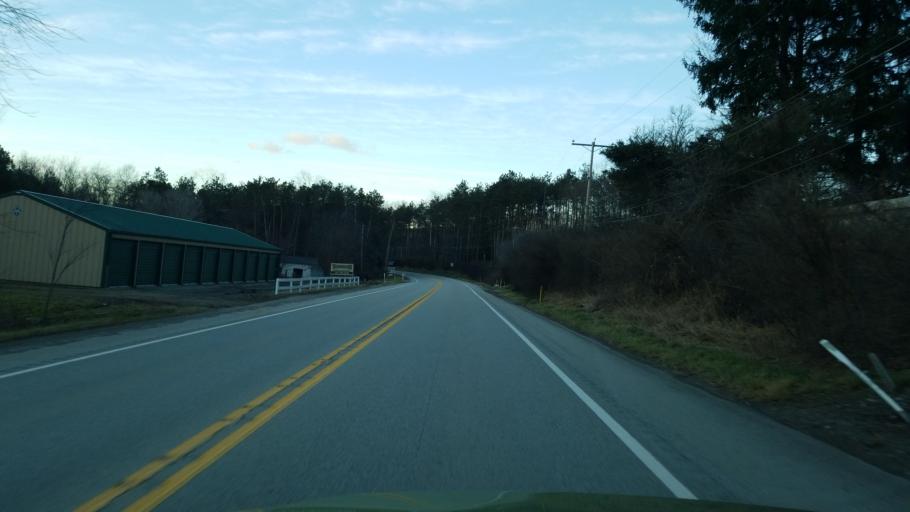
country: US
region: Pennsylvania
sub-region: Indiana County
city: Chevy Chase Heights
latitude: 40.7157
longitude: -79.1019
